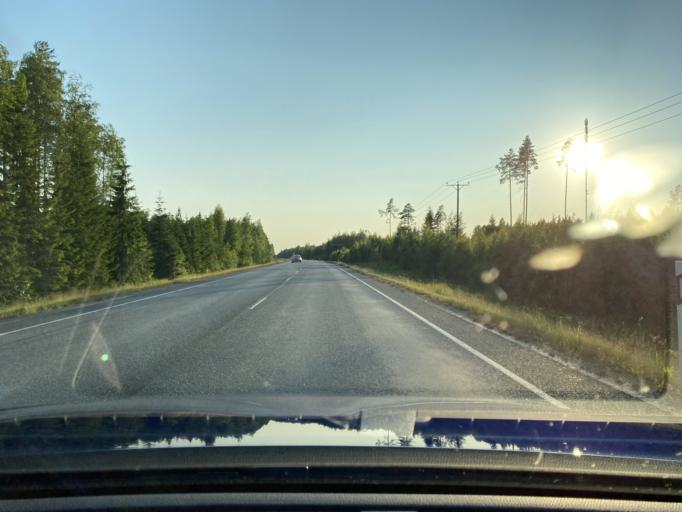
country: FI
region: Haeme
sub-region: Forssa
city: Tammela
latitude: 60.8298
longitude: 23.8727
